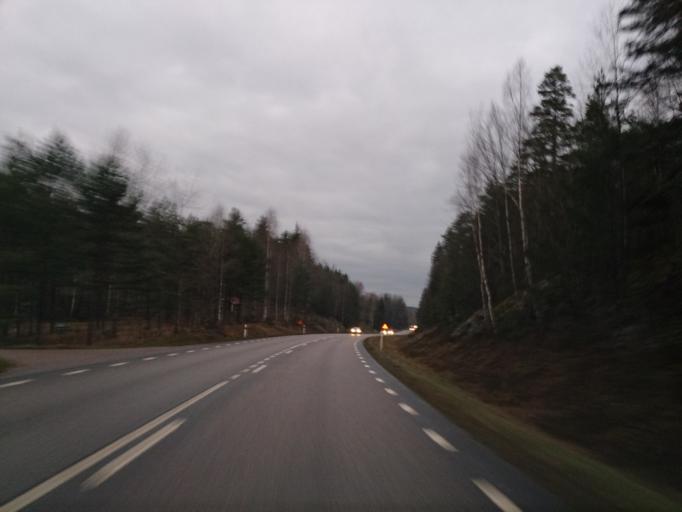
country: SE
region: OEstergoetland
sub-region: Atvidabergs Kommun
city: Atvidaberg
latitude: 58.2423
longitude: 15.9345
